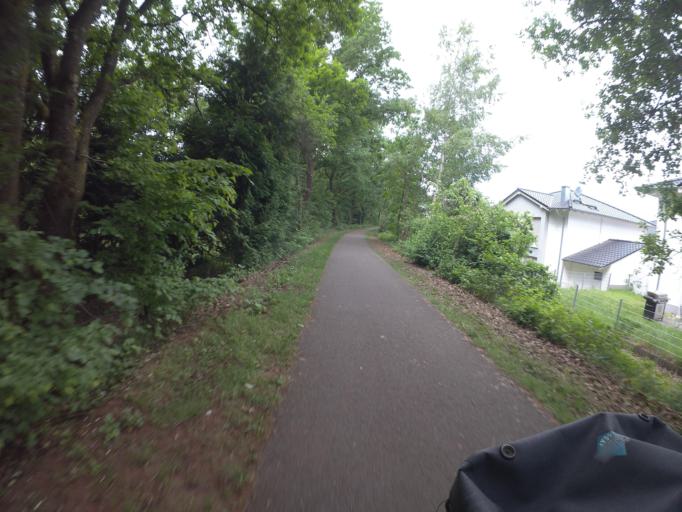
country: DE
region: Rheinland-Pfalz
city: Schwedelbach
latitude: 49.4925
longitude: 7.5912
